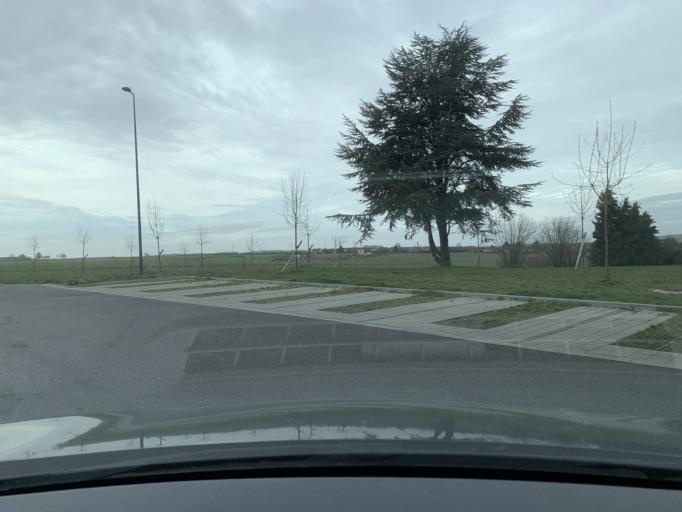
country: FR
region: Nord-Pas-de-Calais
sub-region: Departement du Nord
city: Cambrai
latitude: 50.1569
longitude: 3.2214
